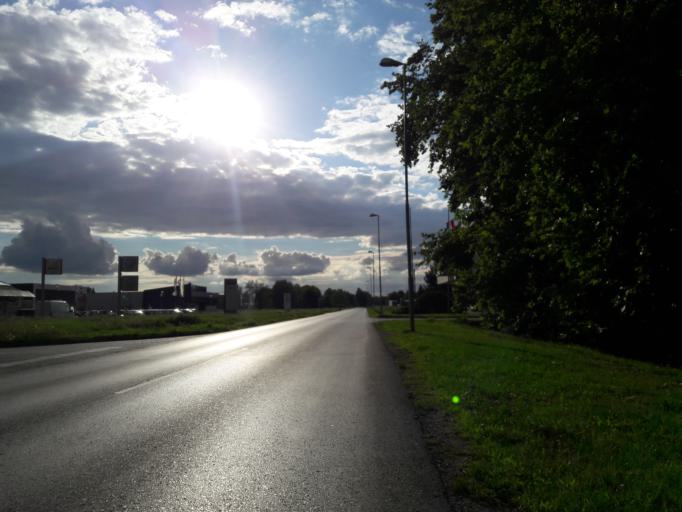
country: HR
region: Osjecko-Baranjska
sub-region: Grad Osijek
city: Osijek
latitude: 45.5434
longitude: 18.7388
